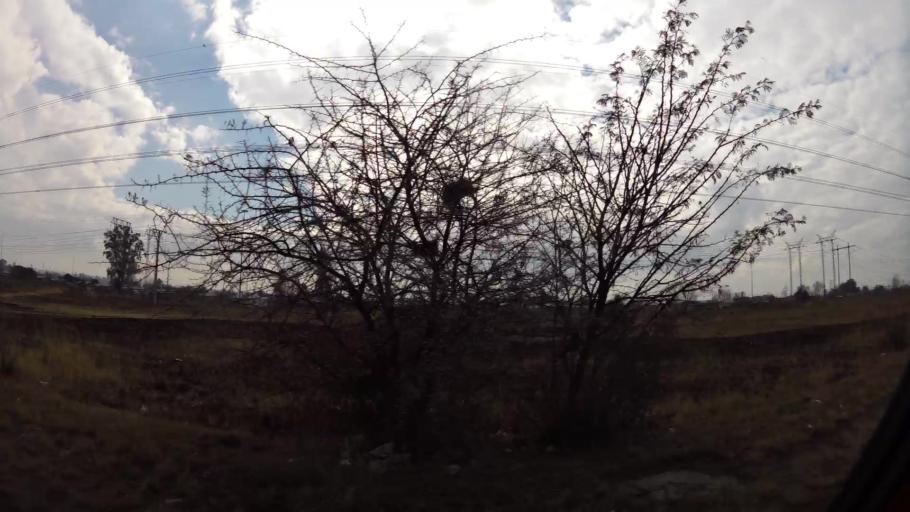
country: ZA
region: Gauteng
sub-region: Sedibeng District Municipality
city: Vanderbijlpark
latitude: -26.6798
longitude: 27.8482
